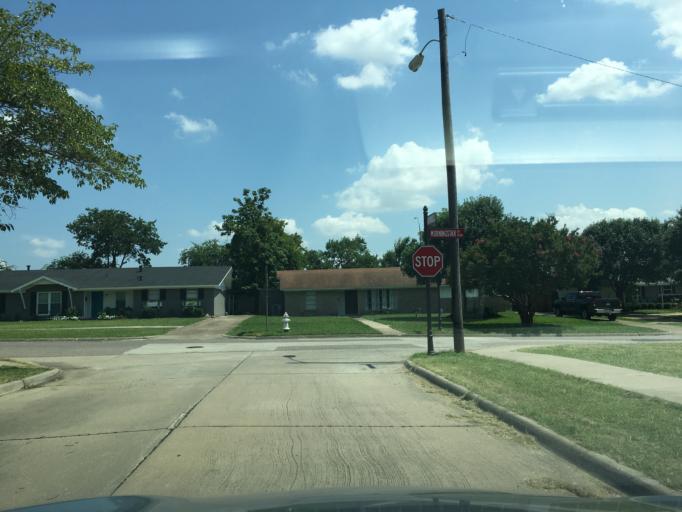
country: US
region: Texas
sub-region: Dallas County
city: Farmers Branch
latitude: 32.9189
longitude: -96.8595
